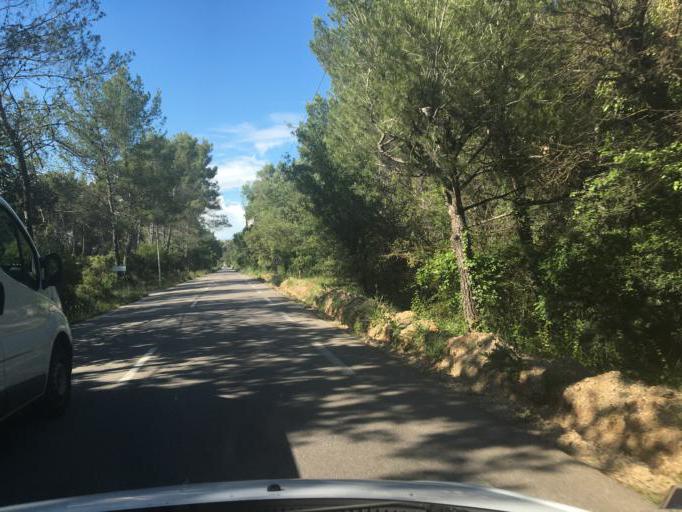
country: FR
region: Provence-Alpes-Cote d'Azur
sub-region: Departement des Bouches-du-Rhone
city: Eguilles
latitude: 43.5250
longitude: 5.3517
